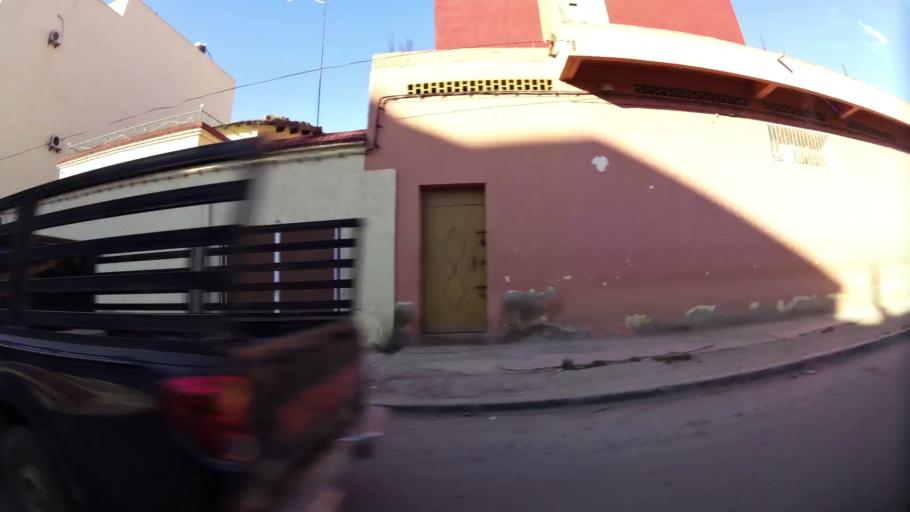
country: MA
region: Oriental
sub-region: Berkane-Taourirt
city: Berkane
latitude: 34.9266
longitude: -2.3351
